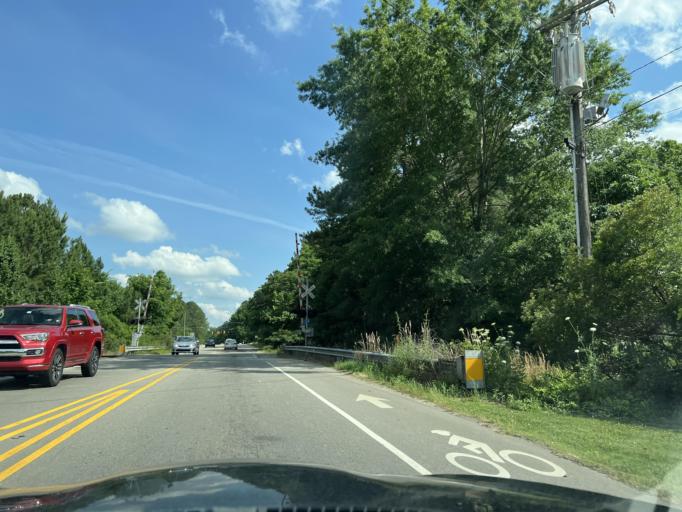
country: US
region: North Carolina
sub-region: Durham County
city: Durham
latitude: 35.9325
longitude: -78.8873
